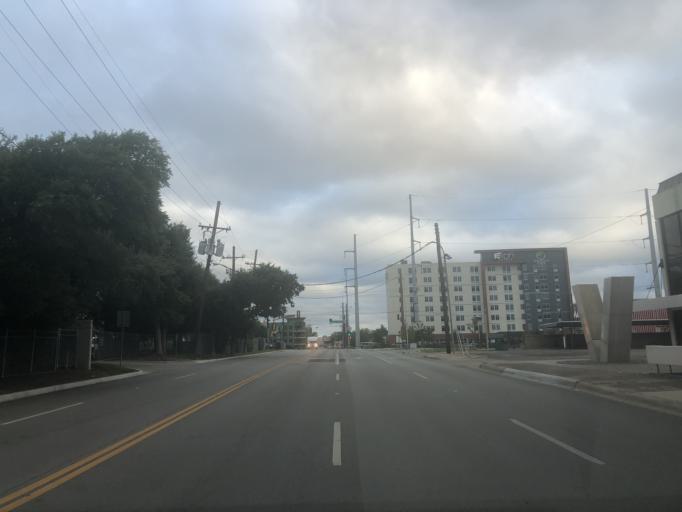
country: US
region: Texas
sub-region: Dallas County
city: University Park
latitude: 32.8248
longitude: -96.8466
